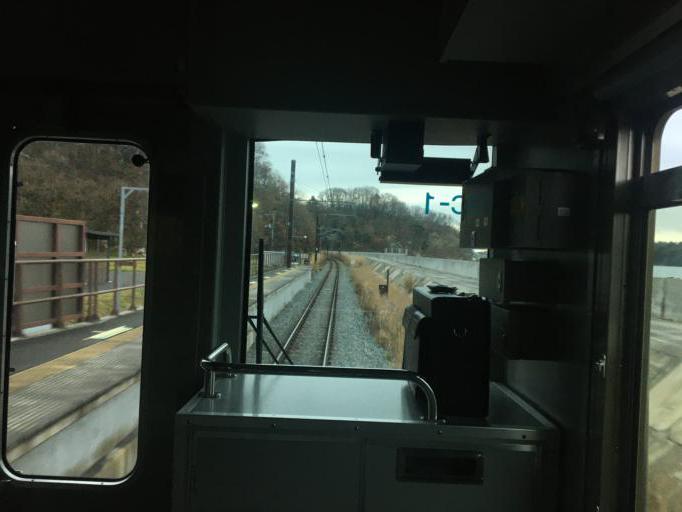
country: JP
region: Miyagi
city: Matsushima
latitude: 38.3864
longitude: 141.1072
